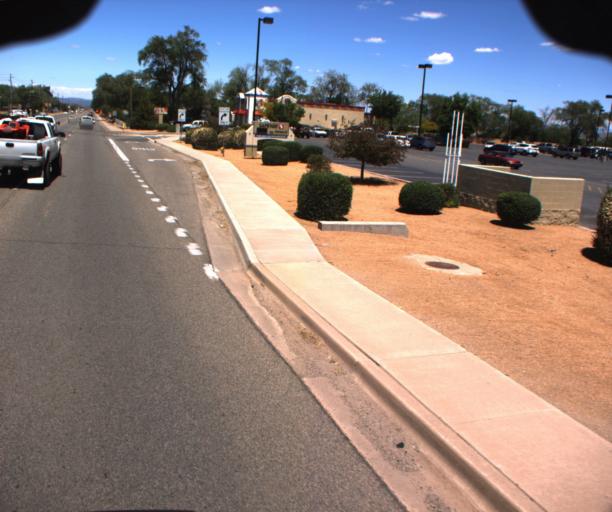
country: US
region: Arizona
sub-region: Yavapai County
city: Chino Valley
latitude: 34.7607
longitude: -112.4536
